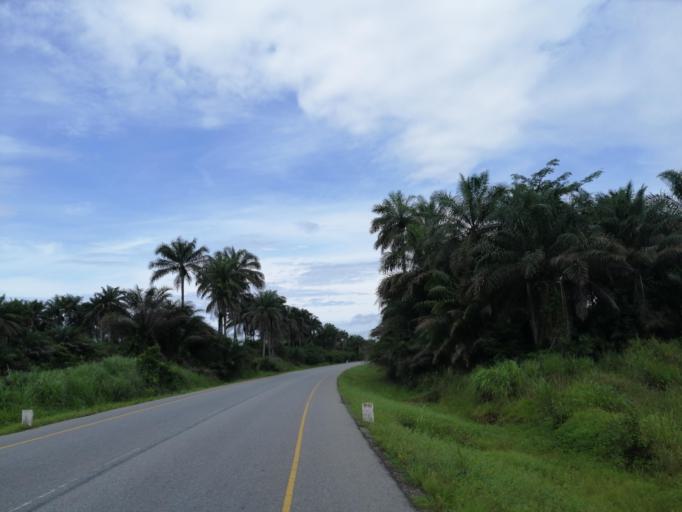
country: SL
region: Northern Province
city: Port Loko
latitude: 8.7586
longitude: -12.9109
